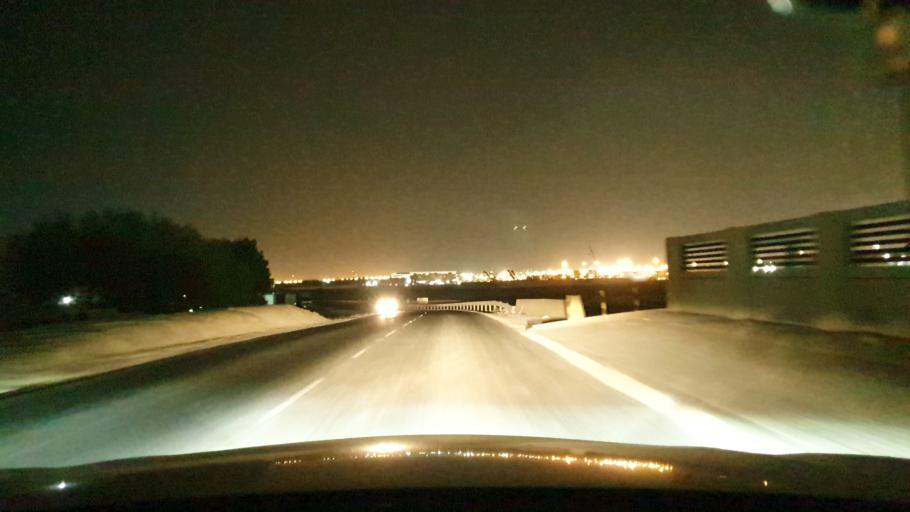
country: BH
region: Northern
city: Sitrah
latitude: 26.0955
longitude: 50.6149
